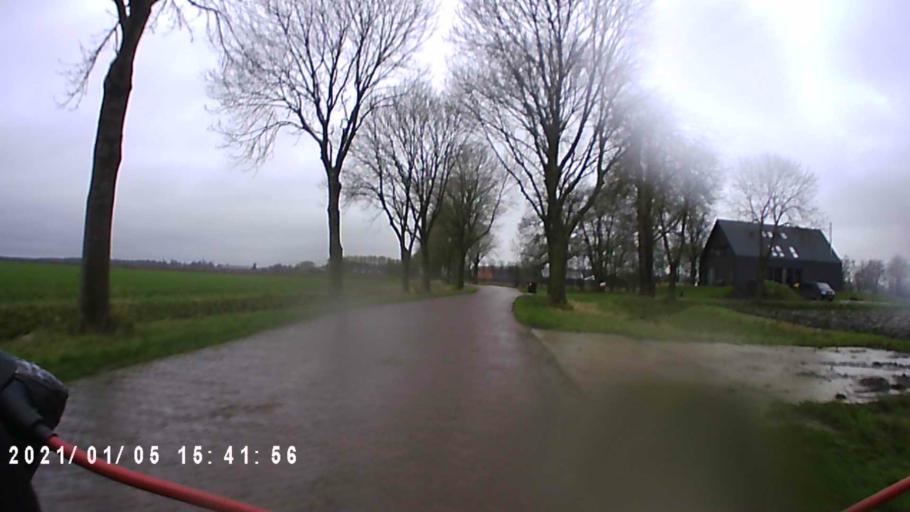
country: NL
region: Groningen
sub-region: Gemeente  Oldambt
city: Winschoten
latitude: 53.2087
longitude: 7.1346
